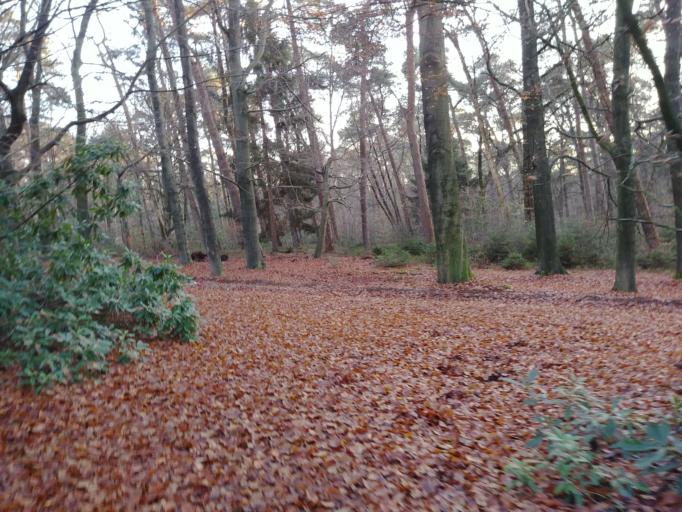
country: NL
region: Utrecht
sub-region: Gemeente Utrechtse Heuvelrug
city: Maarsbergen
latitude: 52.0408
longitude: 5.4022
